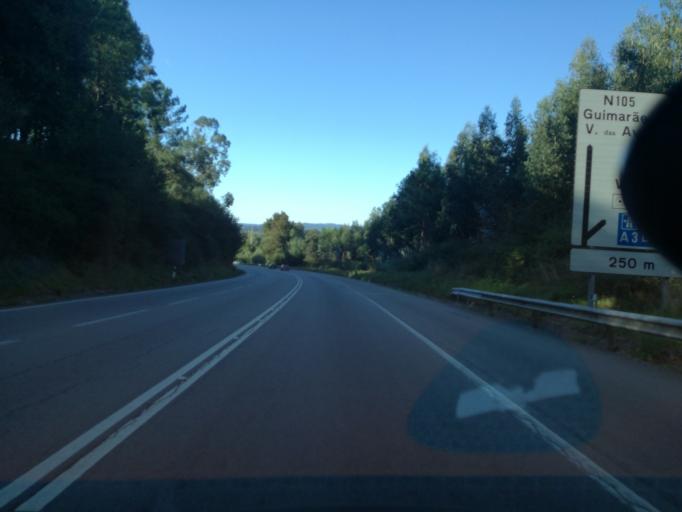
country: PT
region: Porto
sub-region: Santo Tirso
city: Sao Miguel do Couto
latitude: 41.3221
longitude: -8.4689
